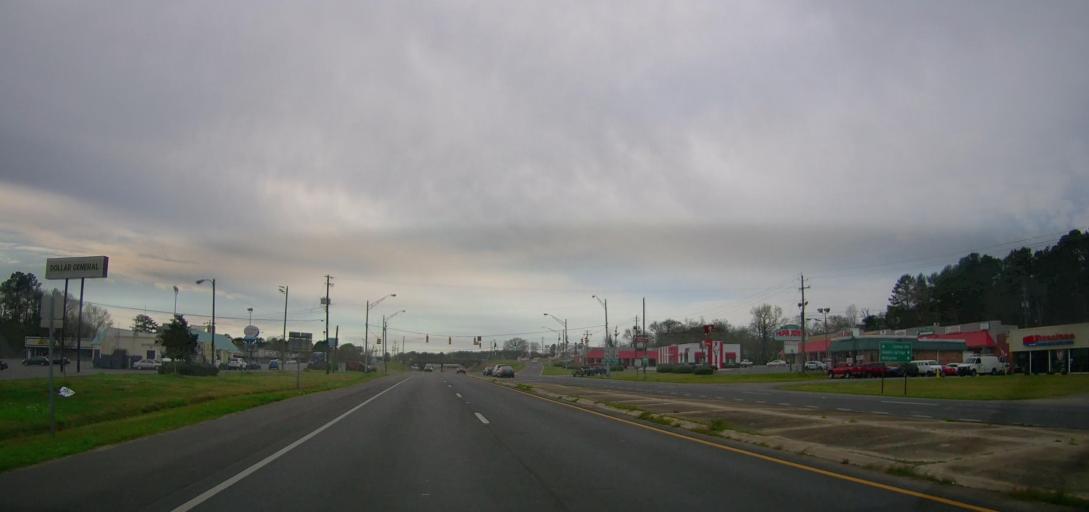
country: US
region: Alabama
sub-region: Walker County
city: Jasper
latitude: 33.8489
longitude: -87.2818
